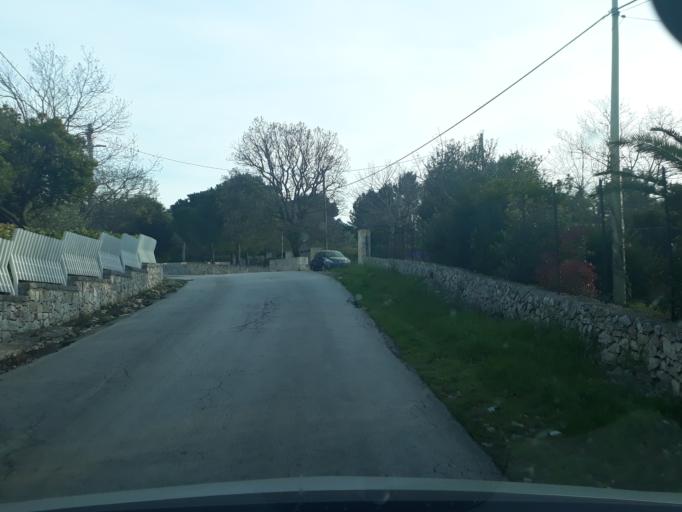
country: IT
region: Apulia
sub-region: Provincia di Brindisi
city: Lamie di Olimpie-Selva
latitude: 40.8283
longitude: 17.3320
